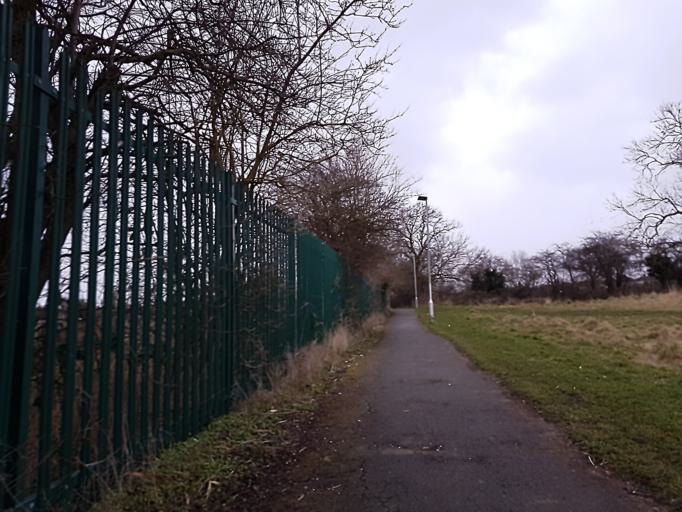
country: GB
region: England
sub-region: North East Lincolnshire
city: Grimbsy
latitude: 53.5588
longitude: -0.1030
